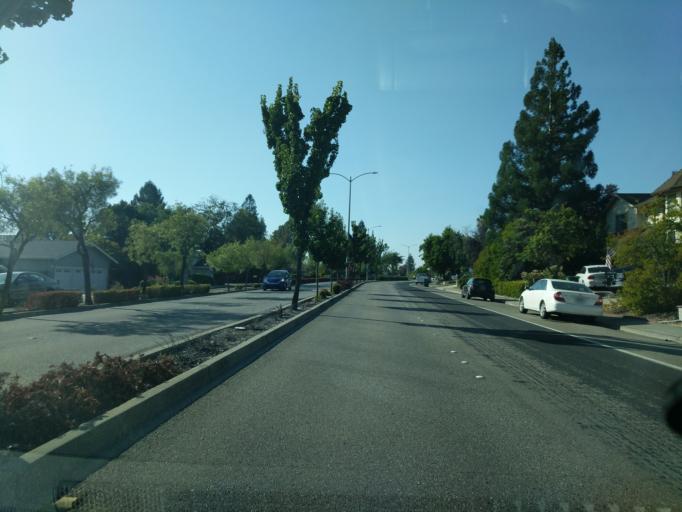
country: US
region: California
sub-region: Alameda County
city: Dublin
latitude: 37.7397
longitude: -121.9271
